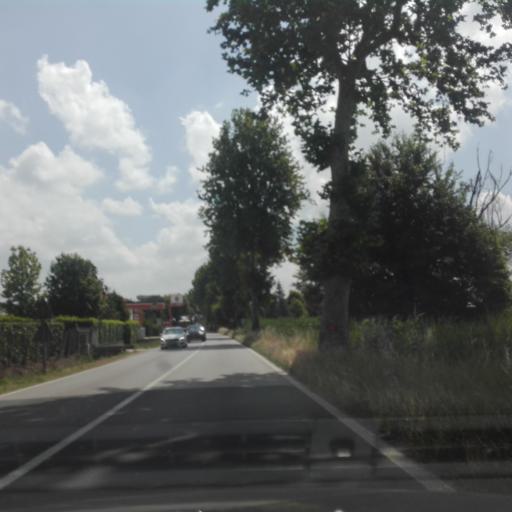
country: IT
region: Veneto
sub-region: Provincia di Rovigo
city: Villadose
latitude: 45.0669
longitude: 11.8947
